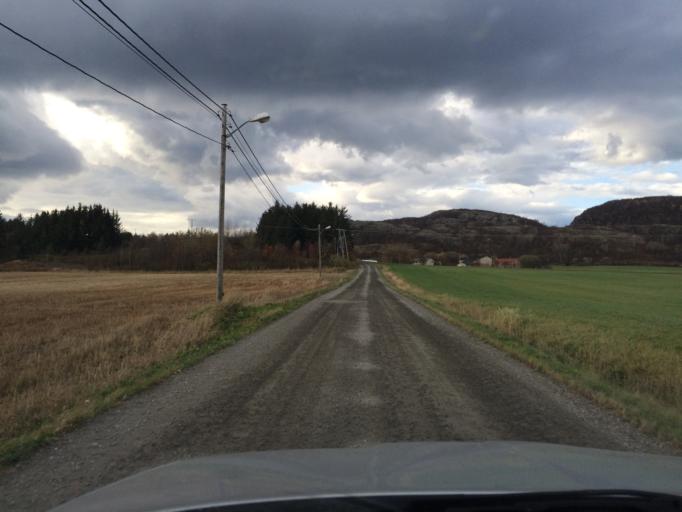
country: NO
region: Nordland
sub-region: Vevelstad
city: Vevelstad
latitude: 65.7722
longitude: 12.4496
